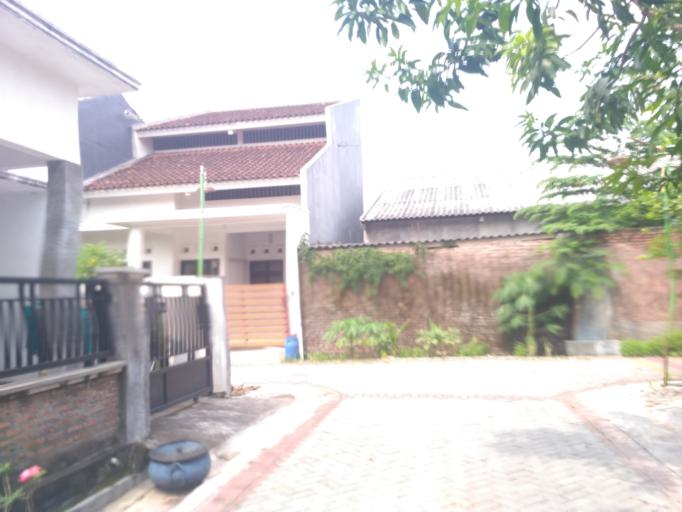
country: ID
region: Central Java
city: Mranggen
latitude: -7.0583
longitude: 110.4678
